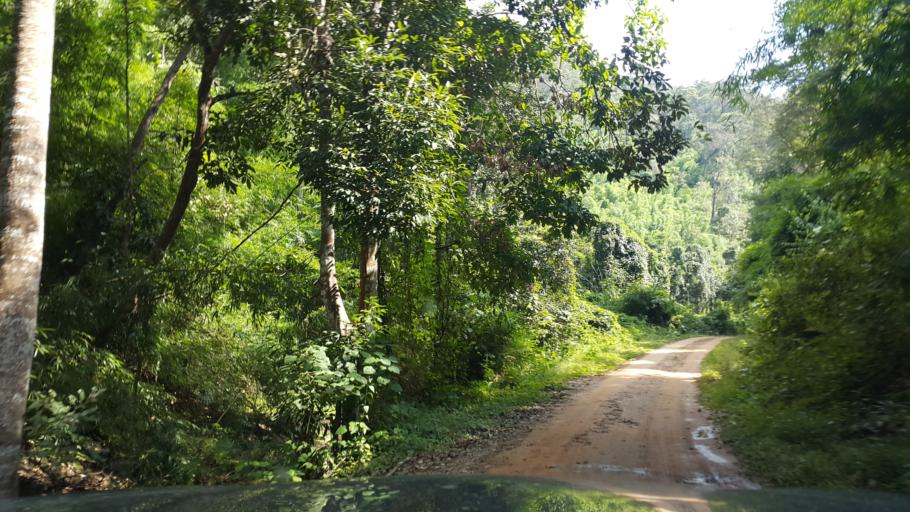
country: TH
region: Chiang Mai
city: Phrao
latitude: 19.0871
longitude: 99.2568
